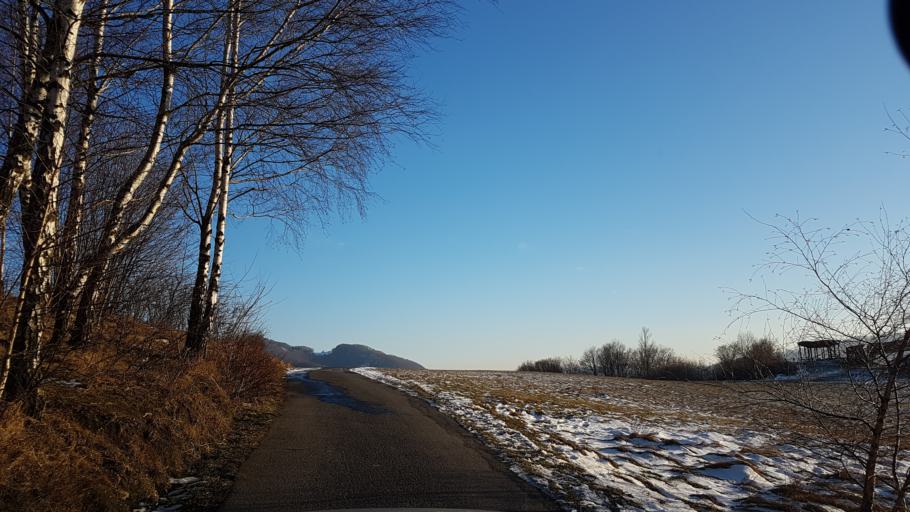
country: PL
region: Lesser Poland Voivodeship
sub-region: Powiat nowosadecki
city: Rytro
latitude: 49.5087
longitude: 20.6724
